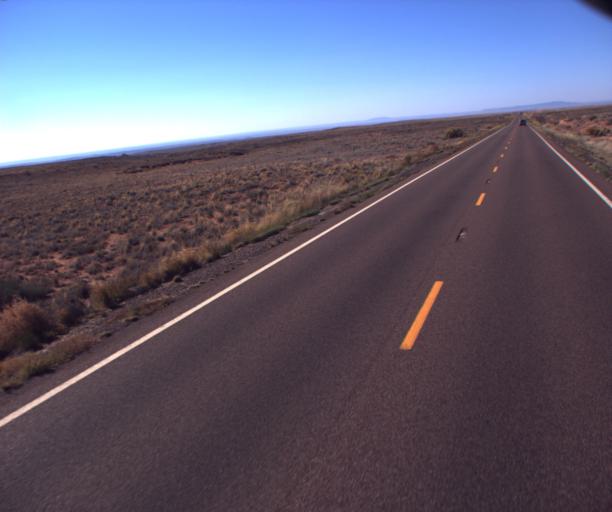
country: US
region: Arizona
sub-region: Navajo County
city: Winslow
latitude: 35.1360
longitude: -110.4897
